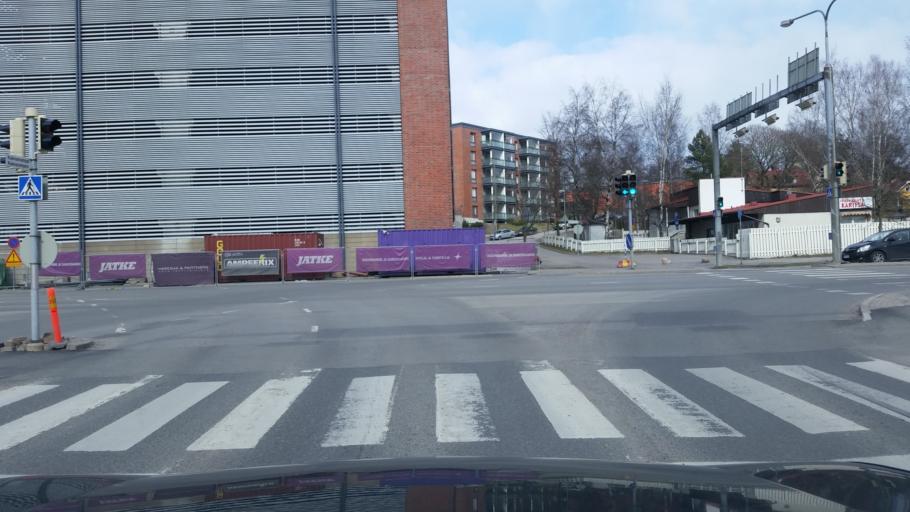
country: FI
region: Varsinais-Suomi
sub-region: Turku
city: Turku
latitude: 60.4506
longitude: 22.3012
